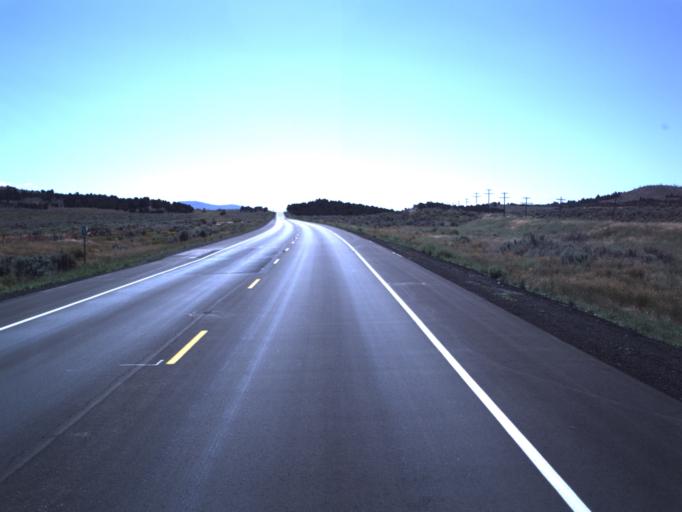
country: US
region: Utah
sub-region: Utah County
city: Genola
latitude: 39.9673
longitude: -112.2536
